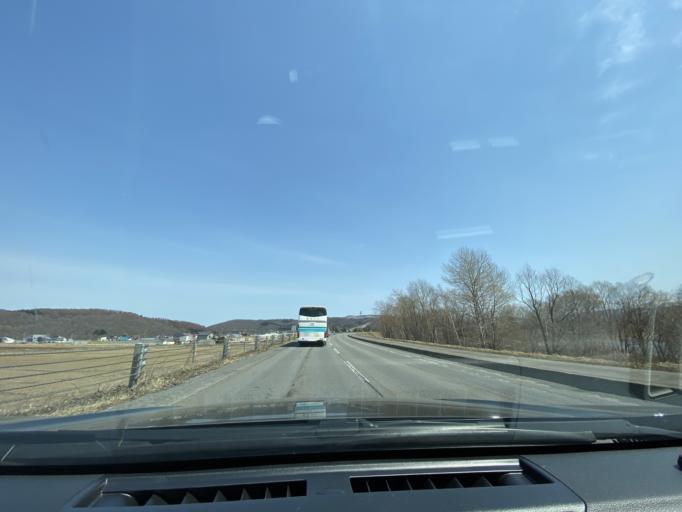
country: JP
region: Hokkaido
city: Kamikawa
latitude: 43.9003
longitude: 142.5577
